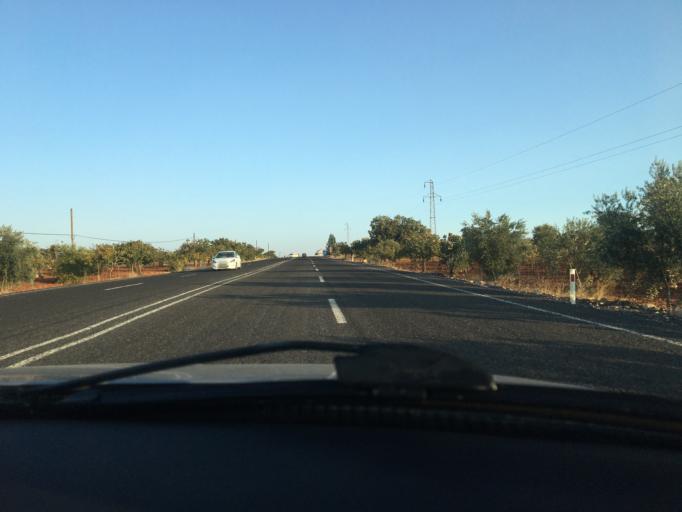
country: TR
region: Sanliurfa
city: Halfeti
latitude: 37.2349
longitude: 37.9314
